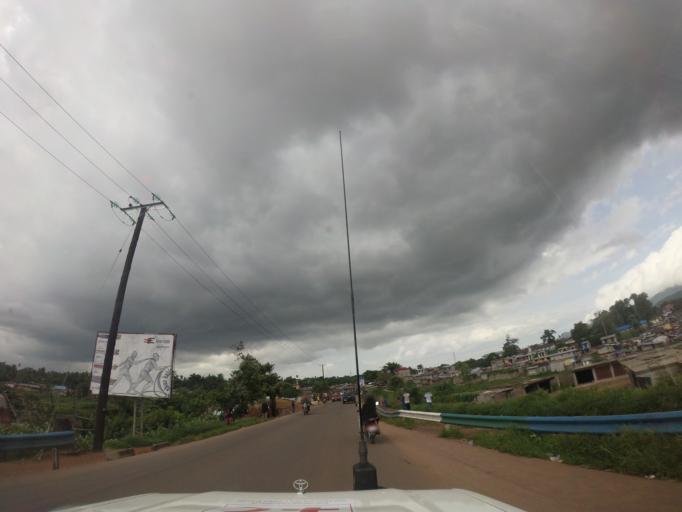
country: SL
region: Western Area
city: Waterloo
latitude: 8.3301
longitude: -13.0697
